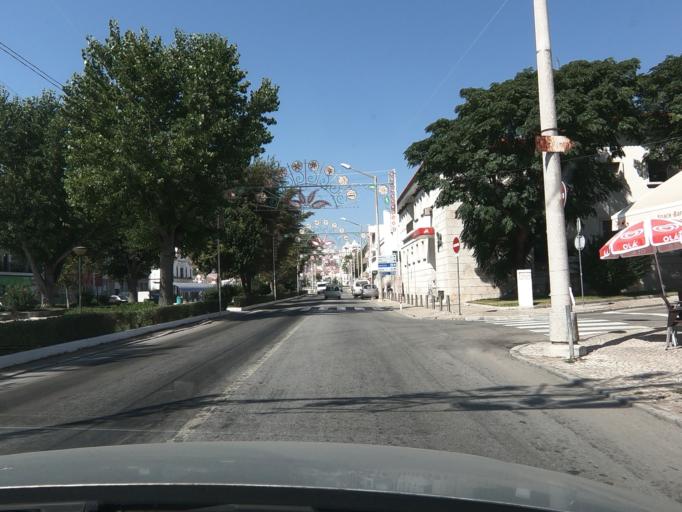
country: PT
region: Setubal
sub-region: Alcacer do Sal
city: Alcacer do Sal
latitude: 38.3695
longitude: -8.5046
